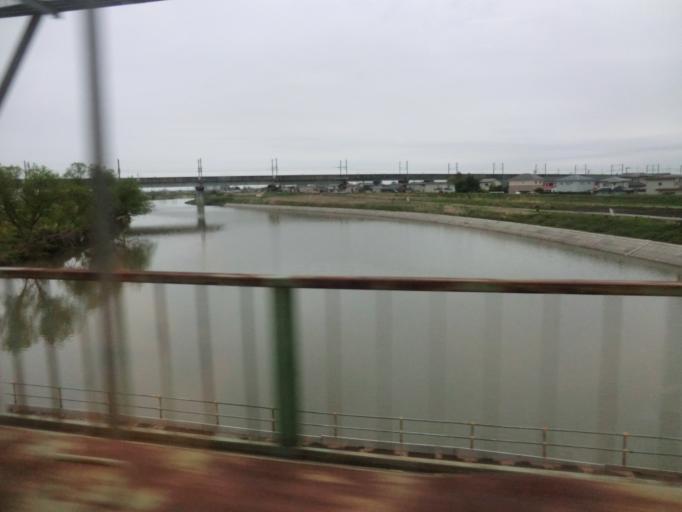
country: JP
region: Miyagi
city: Rifu
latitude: 38.2998
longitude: 140.9516
